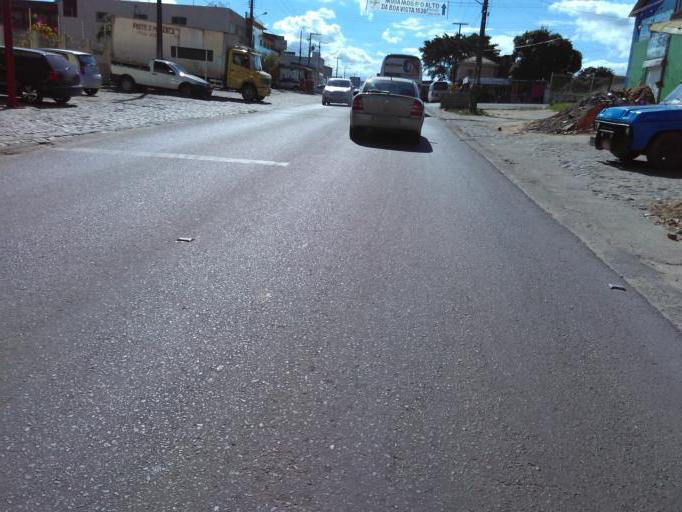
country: BR
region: Sergipe
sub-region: Lagarto
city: Lagarto
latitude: -10.9199
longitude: -37.6730
